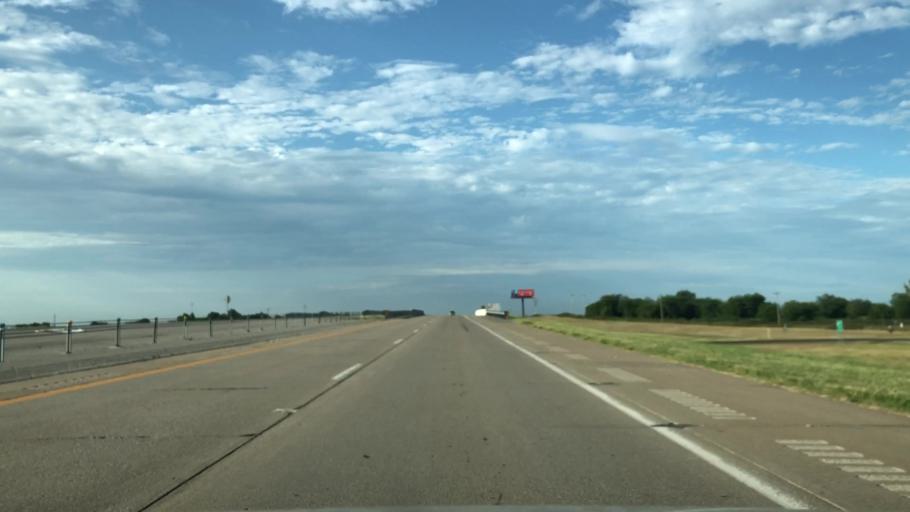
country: US
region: Oklahoma
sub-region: Osage County
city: Skiatook
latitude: 36.3672
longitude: -95.9208
